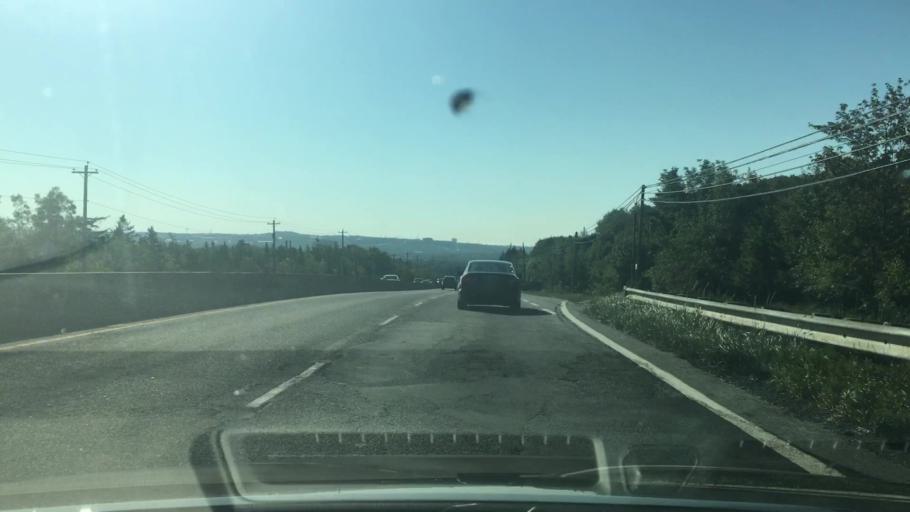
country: CA
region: Nova Scotia
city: Dartmouth
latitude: 44.7135
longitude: -63.6299
